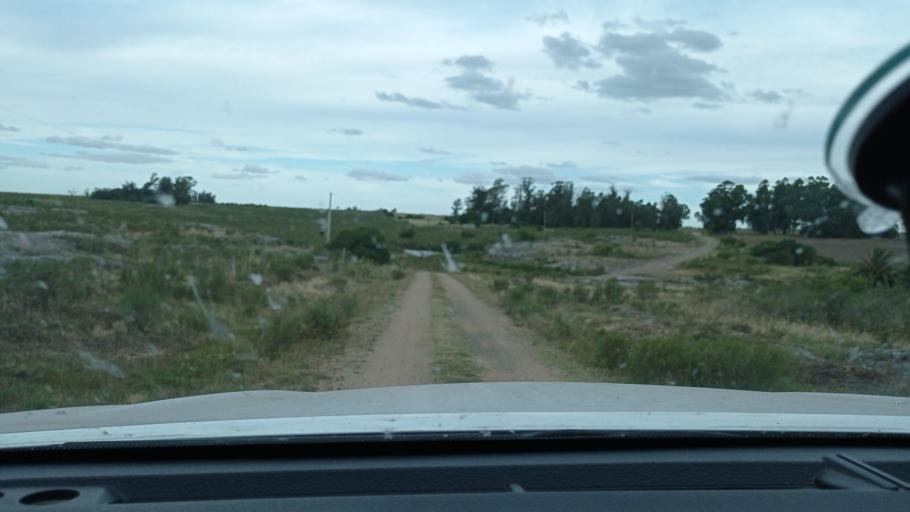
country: UY
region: Florida
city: Casupa
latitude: -34.1424
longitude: -55.7988
